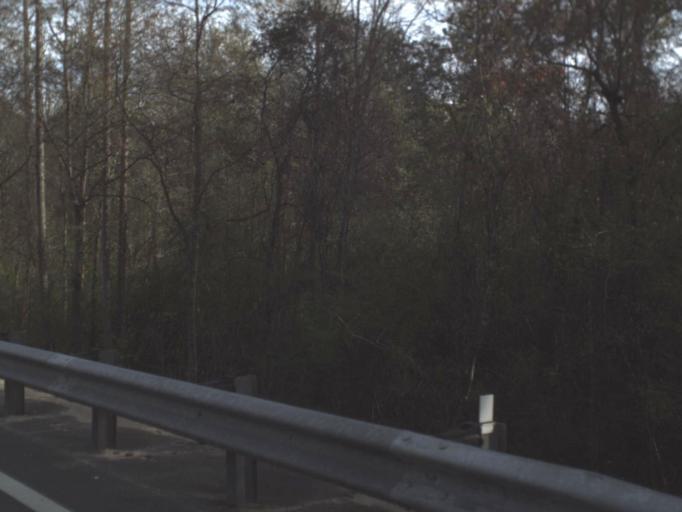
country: US
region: Florida
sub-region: Holmes County
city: Bonifay
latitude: 30.7820
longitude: -85.6476
